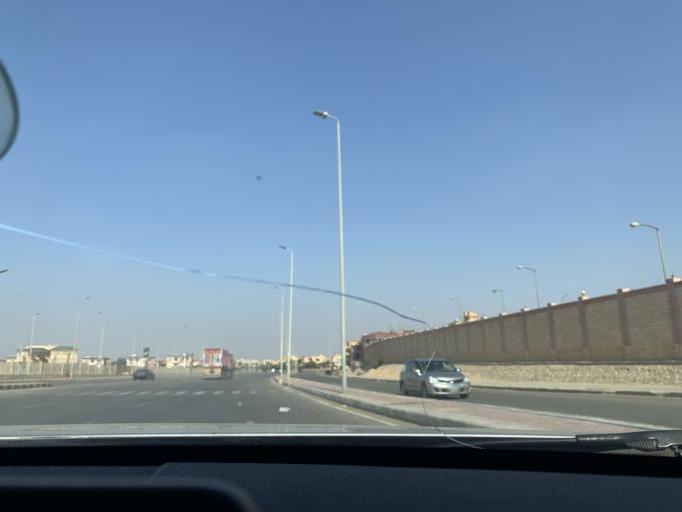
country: EG
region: Muhafazat al Qahirah
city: Cairo
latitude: 30.0066
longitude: 31.4703
